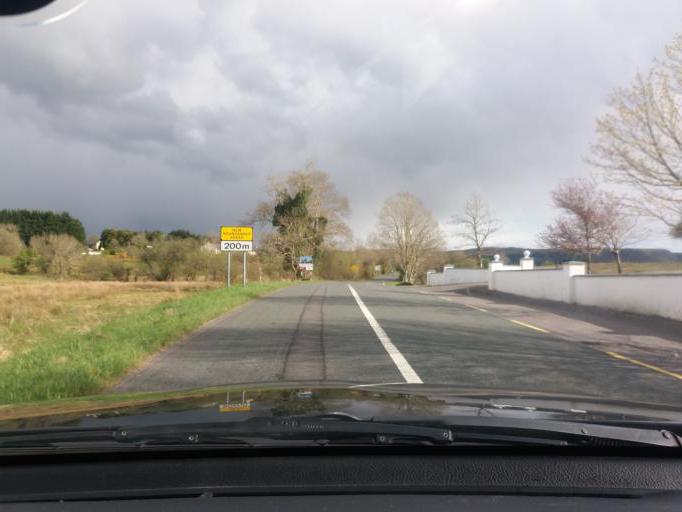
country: IE
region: Connaught
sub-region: County Leitrim
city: Manorhamilton
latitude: 54.3117
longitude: -8.1867
